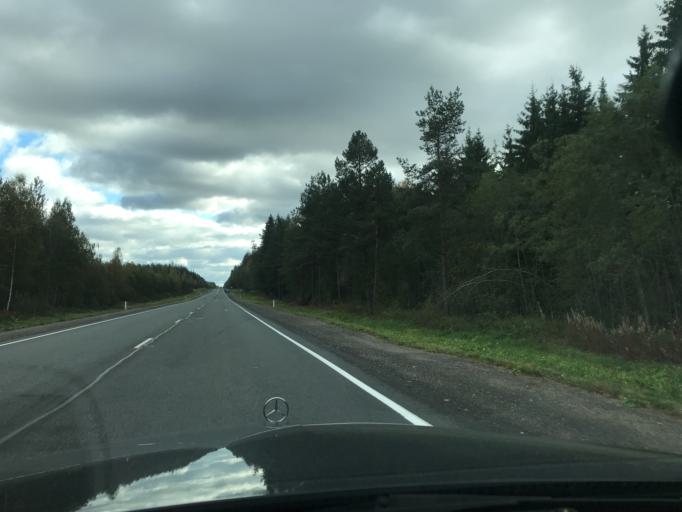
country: RU
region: Pskov
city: Opochka
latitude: 56.9792
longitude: 28.6267
